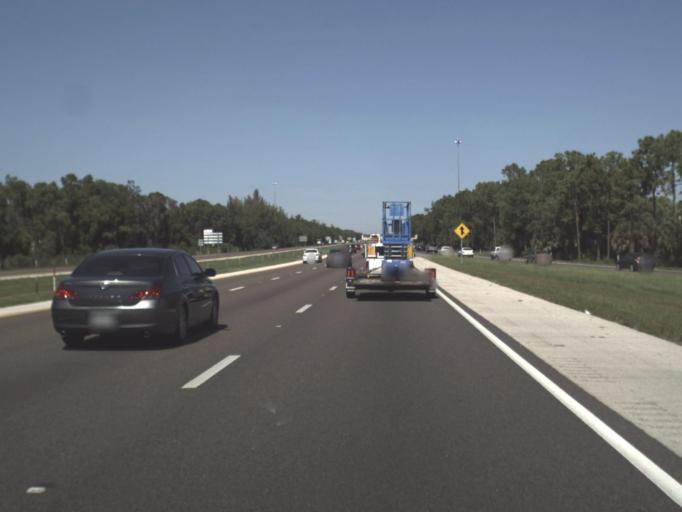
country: US
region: Florida
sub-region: Collier County
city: Vineyards
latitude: 26.2152
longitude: -81.7360
